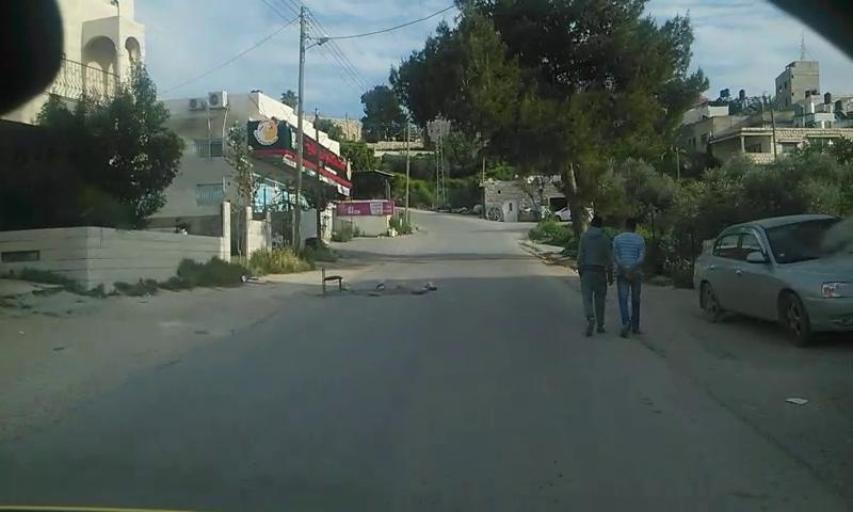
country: PS
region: West Bank
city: Nuba
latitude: 31.6087
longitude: 35.0366
